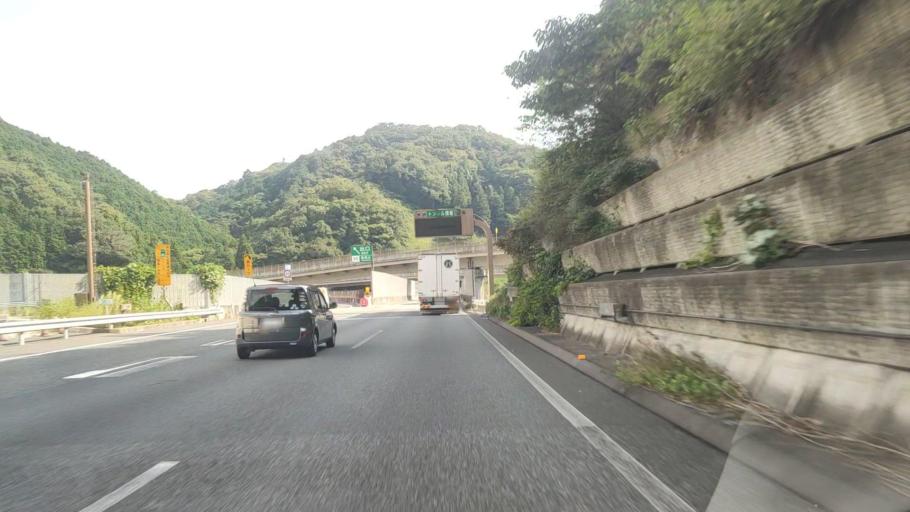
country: JP
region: Tokyo
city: Hachioji
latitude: 35.6268
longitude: 139.2618
